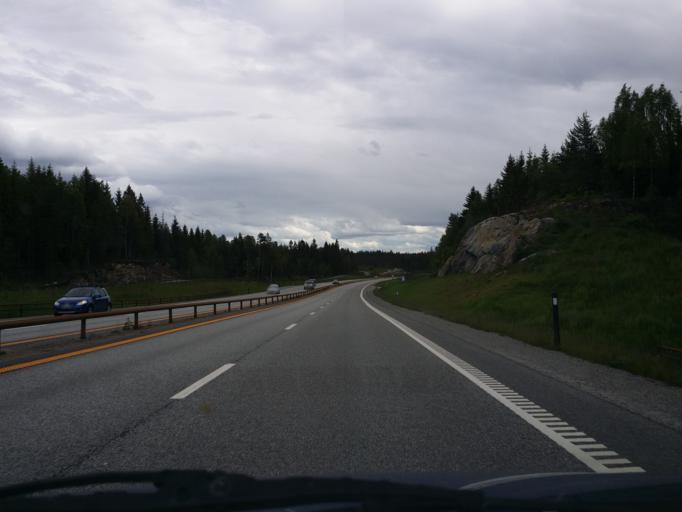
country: NO
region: Akershus
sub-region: Eidsvoll
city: Raholt
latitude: 60.2700
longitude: 11.1585
